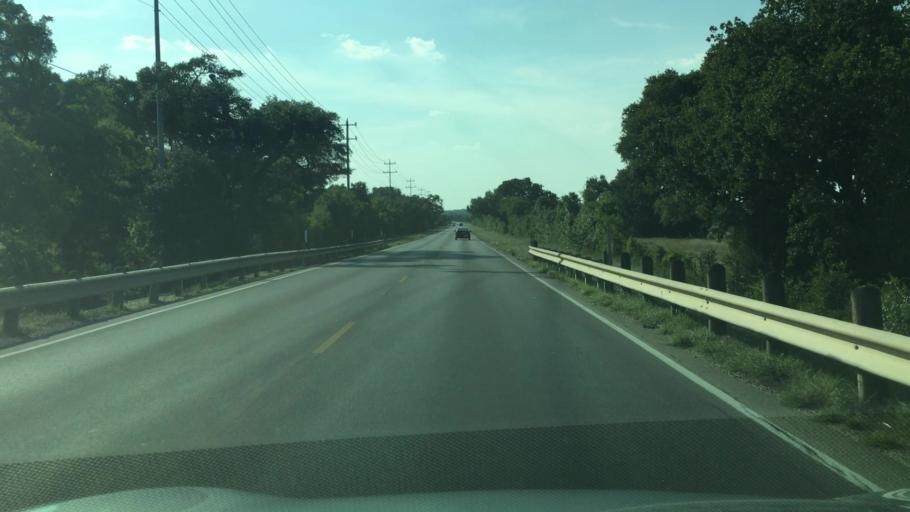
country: US
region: Texas
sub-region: Travis County
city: Shady Hollow
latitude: 30.1061
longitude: -97.9428
